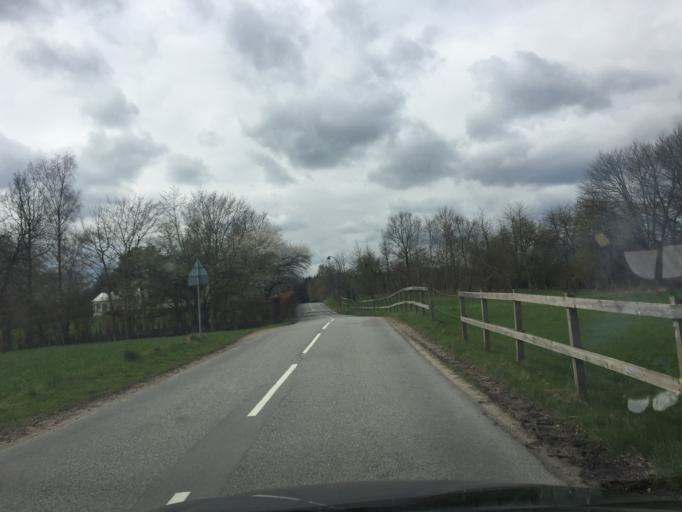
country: DK
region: Capital Region
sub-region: Horsholm Kommune
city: Horsholm
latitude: 55.8484
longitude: 12.4955
